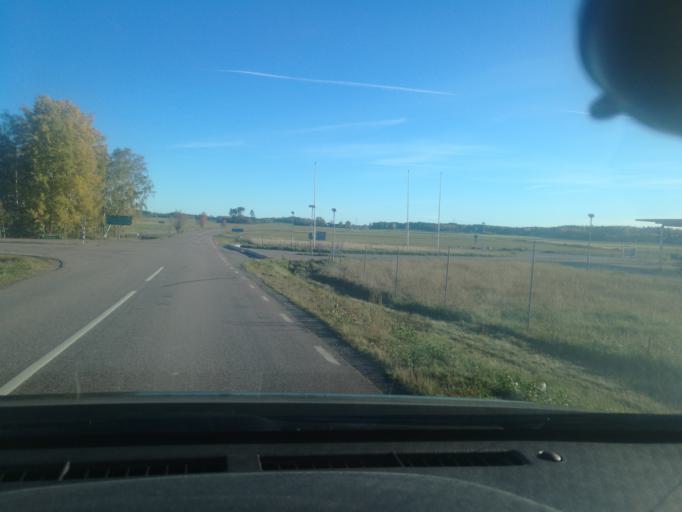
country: SE
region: Vaestmanland
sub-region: Kopings Kommun
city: Koping
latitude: 59.5692
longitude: 16.0915
